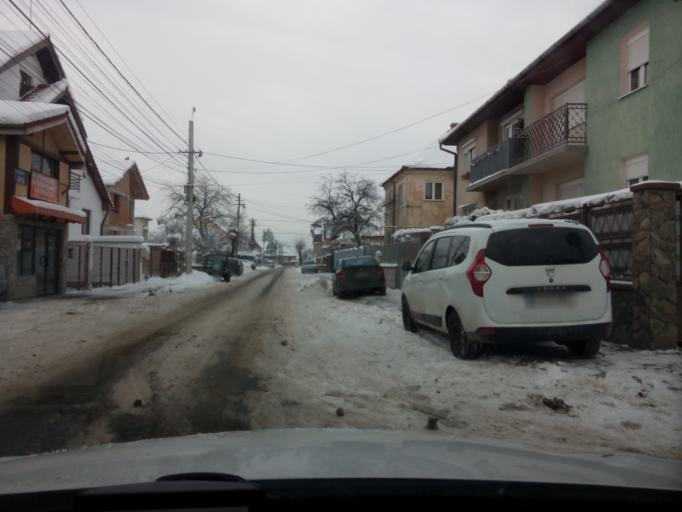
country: RO
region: Sibiu
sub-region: Municipiul Sibiu
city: Sibiu
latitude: 45.7876
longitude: 24.1665
